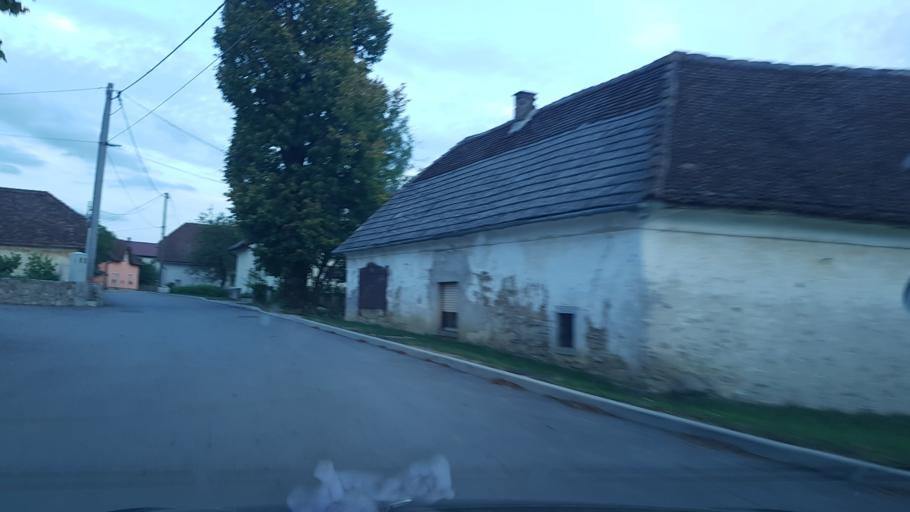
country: SI
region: Postojna
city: Postojna
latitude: 45.7514
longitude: 14.1785
